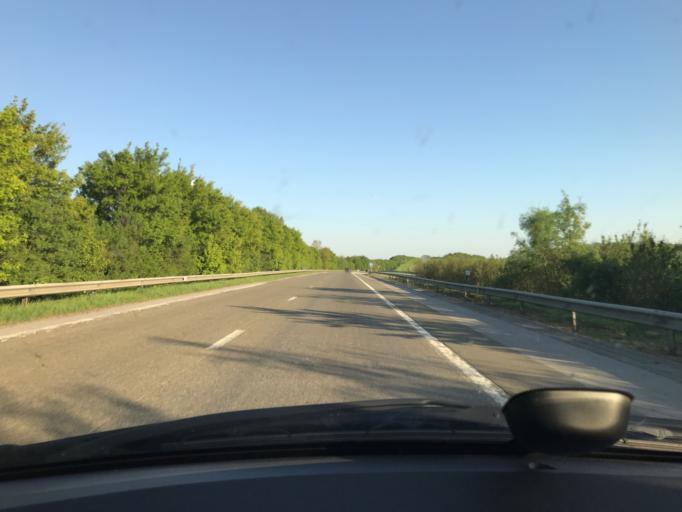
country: BE
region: Wallonia
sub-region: Province de Namur
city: Ciney
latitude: 50.2587
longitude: 5.0443
